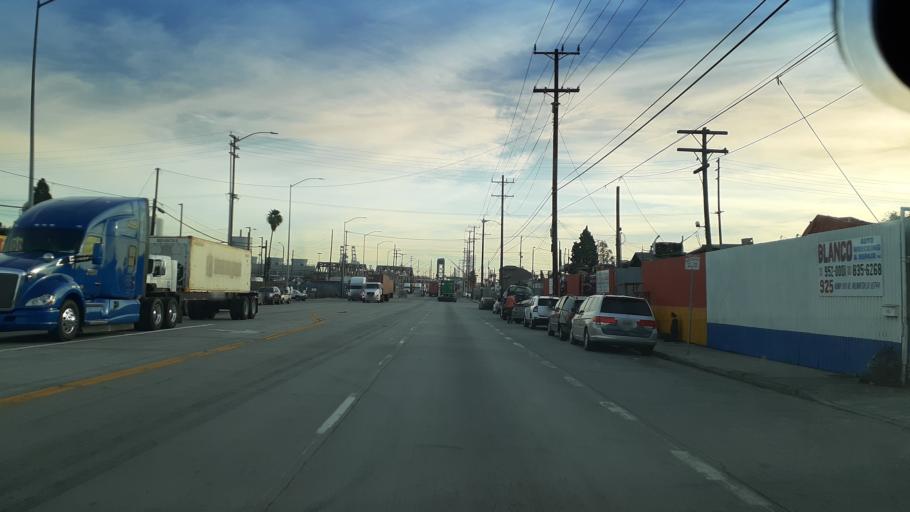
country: US
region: California
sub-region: Los Angeles County
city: Long Beach
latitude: 33.7833
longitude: -118.2421
